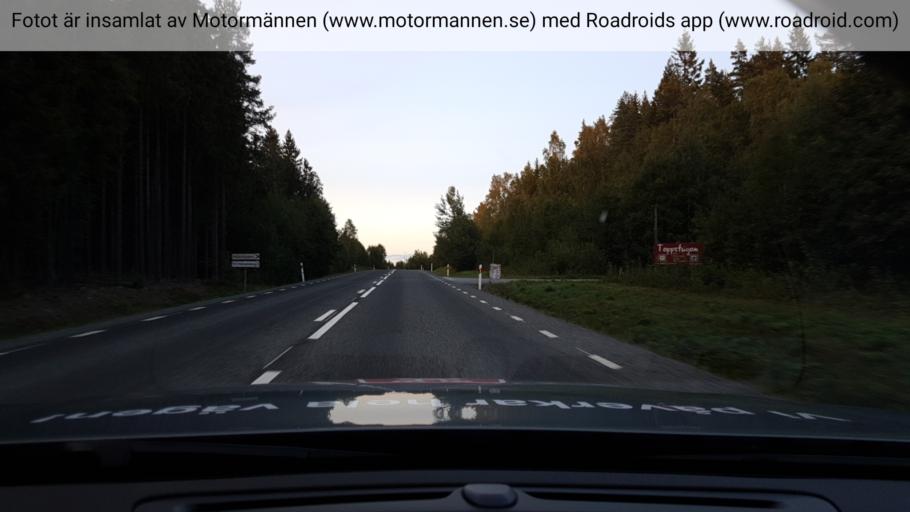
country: SE
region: OErebro
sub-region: Hallefors Kommun
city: Haellefors
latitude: 59.7970
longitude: 14.5508
